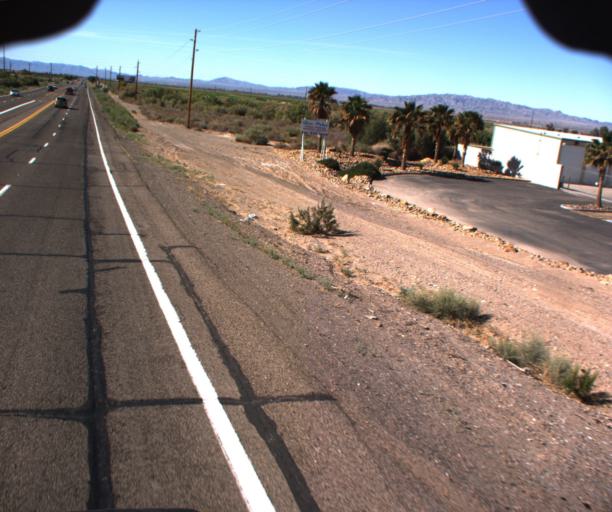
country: US
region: Arizona
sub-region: Mohave County
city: Mohave Valley
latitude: 34.9721
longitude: -114.5980
